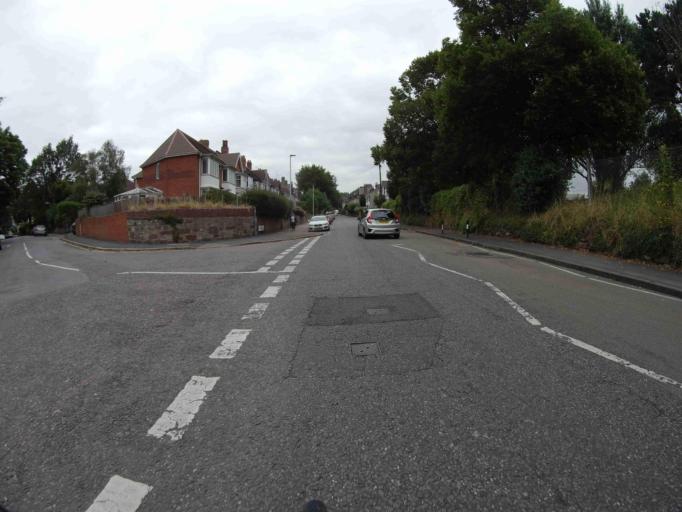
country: GB
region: England
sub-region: Devon
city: Exeter
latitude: 50.7322
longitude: -3.5180
